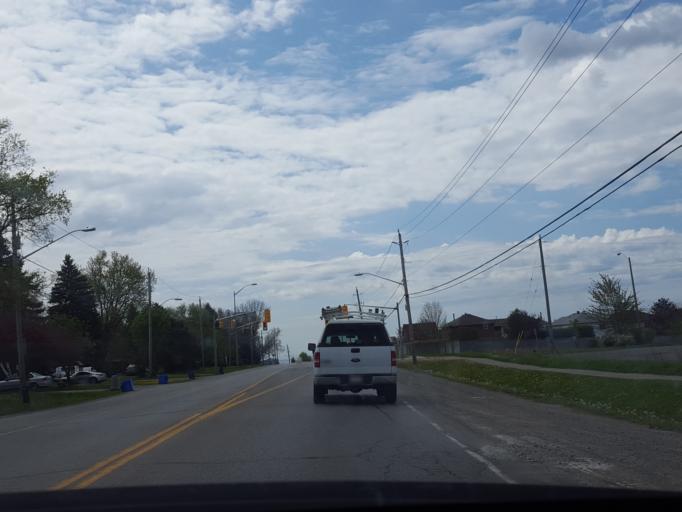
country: CA
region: Ontario
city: Oshawa
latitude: 43.9079
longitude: -78.7007
